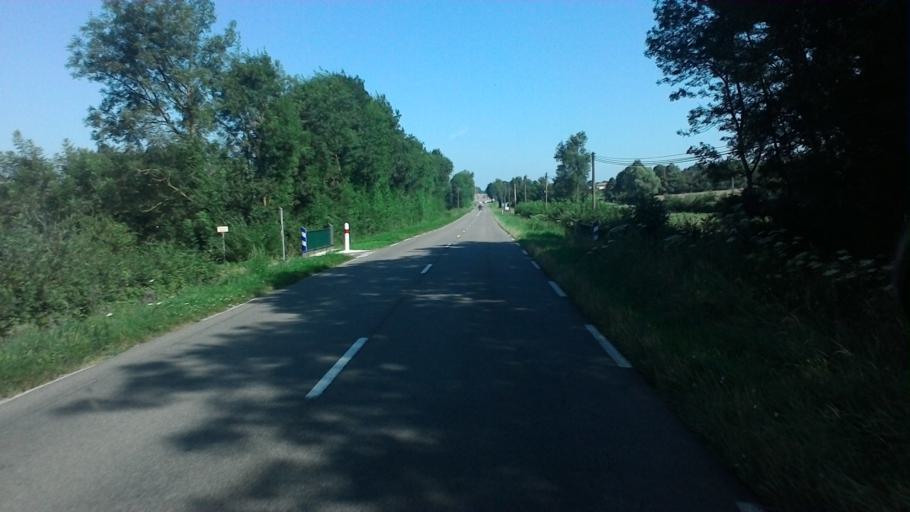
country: FR
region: Rhone-Alpes
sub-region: Departement de l'Ain
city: Saint-Trivier-de-Courtes
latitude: 46.4173
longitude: 5.1022
